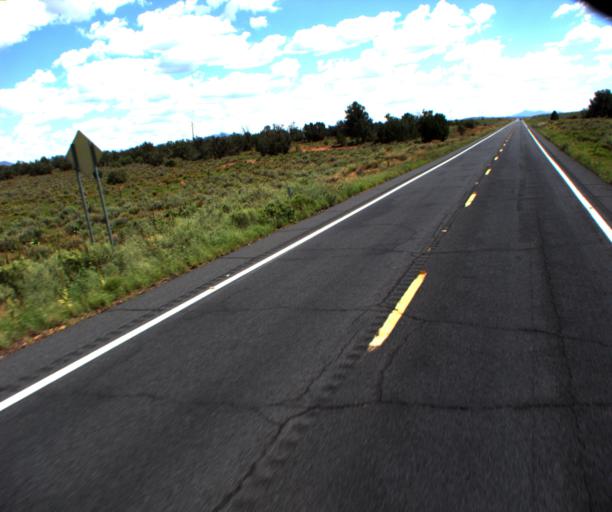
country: US
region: Arizona
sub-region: Coconino County
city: Williams
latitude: 35.6385
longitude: -112.1413
